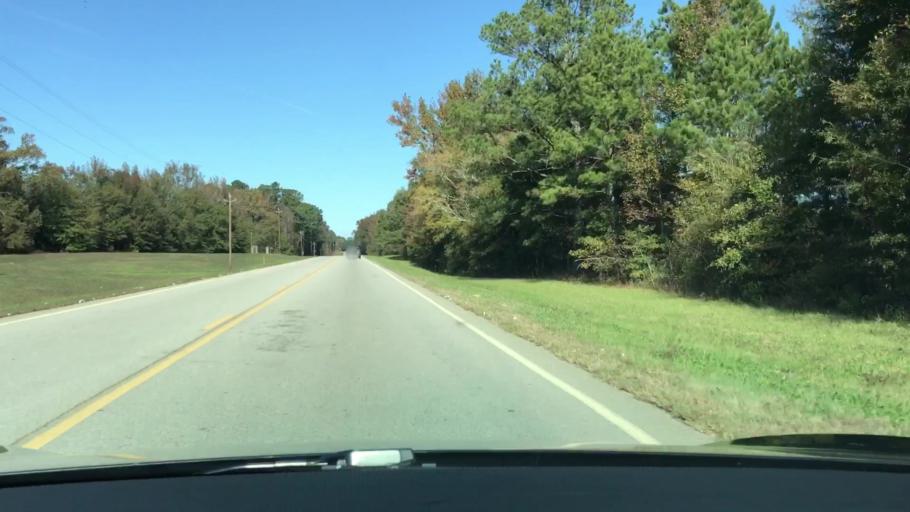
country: US
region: Georgia
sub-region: Warren County
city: Firing Range
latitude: 33.4279
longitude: -82.6841
